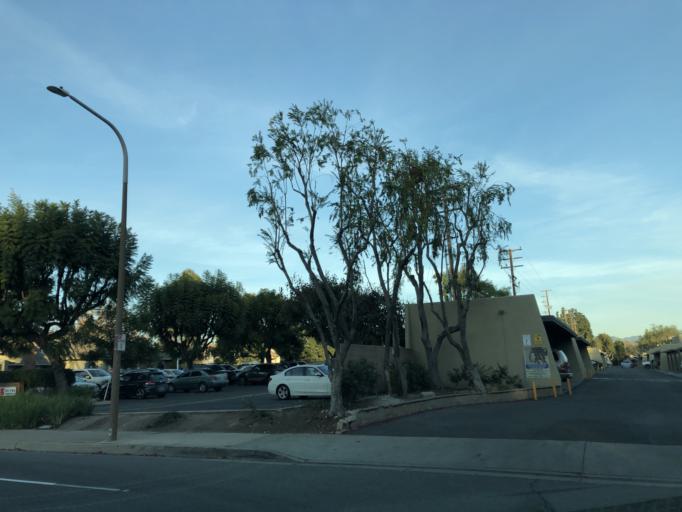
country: US
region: California
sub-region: Orange County
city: Tustin
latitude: 33.7580
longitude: -117.8417
